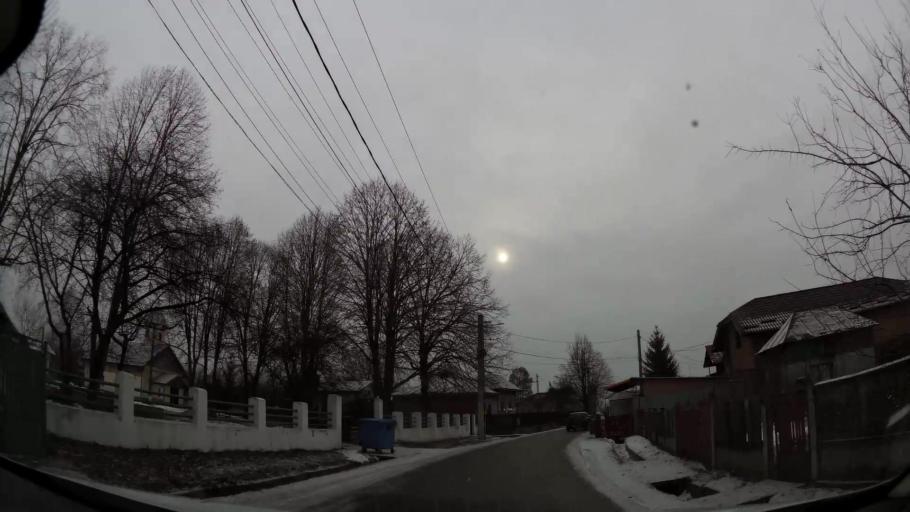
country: RO
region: Dambovita
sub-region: Municipiul Targoviste
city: Targoviste
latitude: 44.9353
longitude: 25.4749
